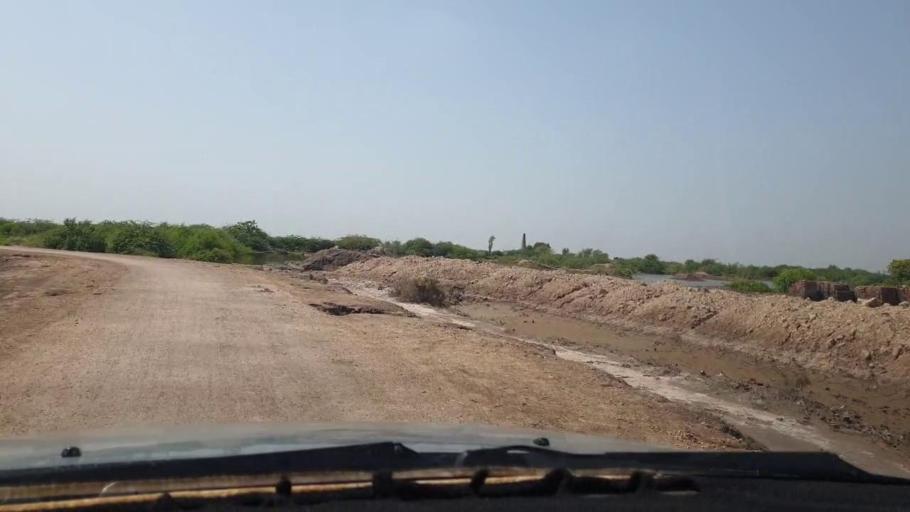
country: PK
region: Sindh
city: Tando Ghulam Ali
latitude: 25.1403
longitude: 68.8198
